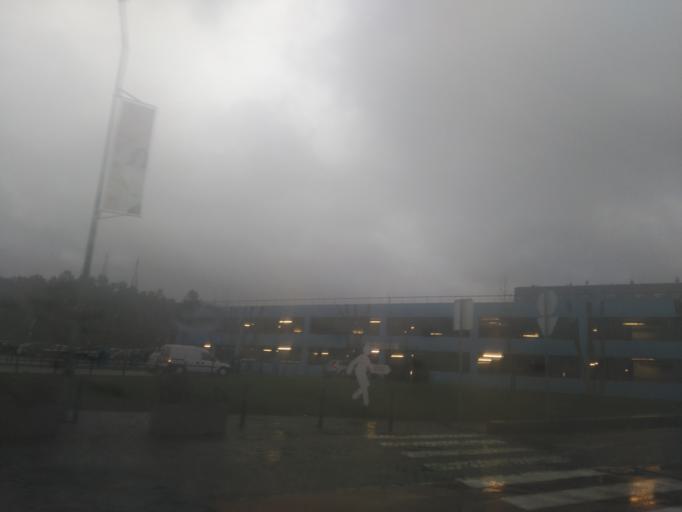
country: PT
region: Braga
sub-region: Braga
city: Adaufe
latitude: 41.5688
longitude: -8.4009
